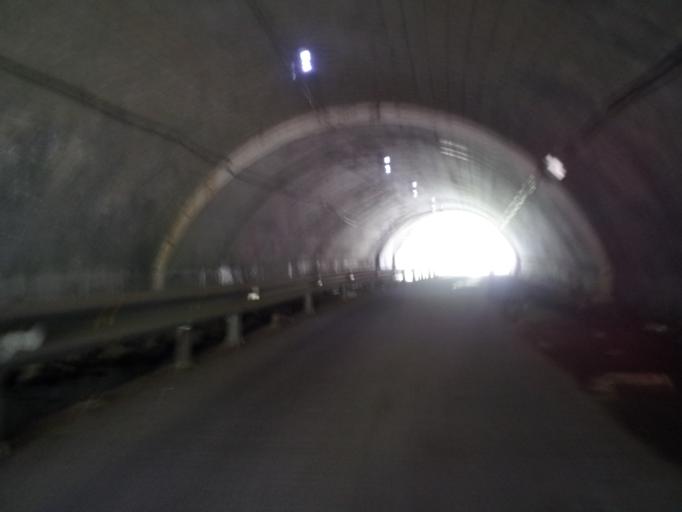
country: KR
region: Daejeon
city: Daejeon
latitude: 36.3355
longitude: 127.4897
